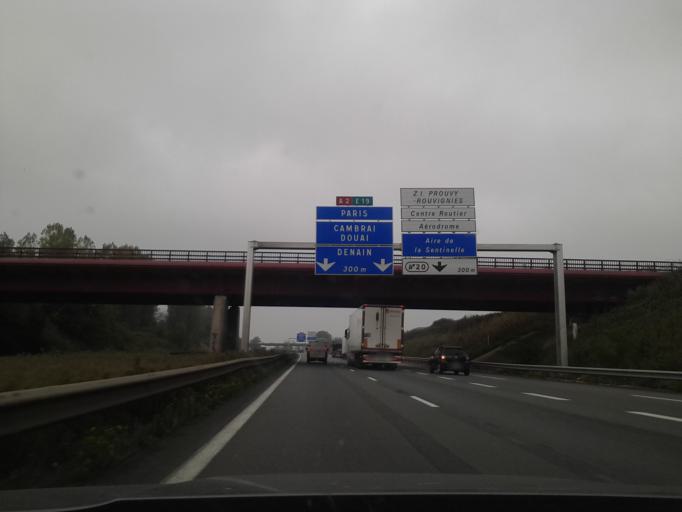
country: FR
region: Nord-Pas-de-Calais
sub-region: Departement du Nord
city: La Sentinelle
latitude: 50.3413
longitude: 3.4814
